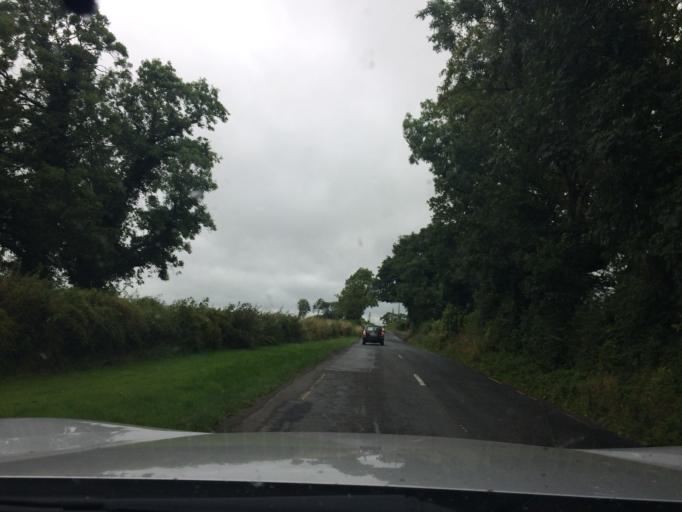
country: IE
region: Munster
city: Cashel
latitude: 52.4848
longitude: -7.8544
